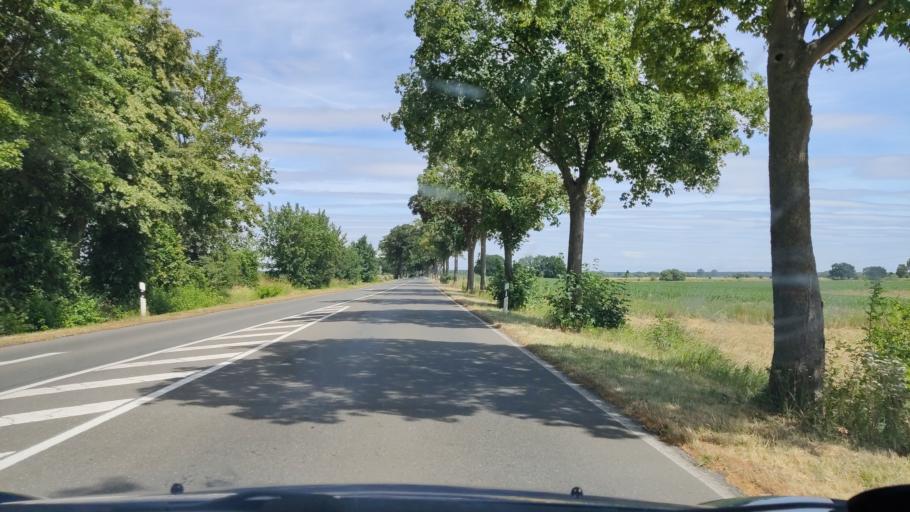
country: DE
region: Lower Saxony
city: Neustadt am Rubenberge
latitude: 52.5180
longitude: 9.4652
